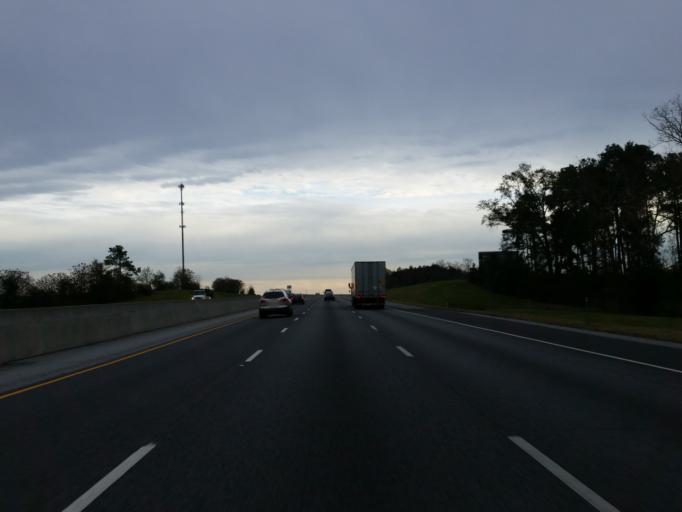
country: US
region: Georgia
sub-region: Turner County
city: Ashburn
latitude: 31.6223
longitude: -83.5731
